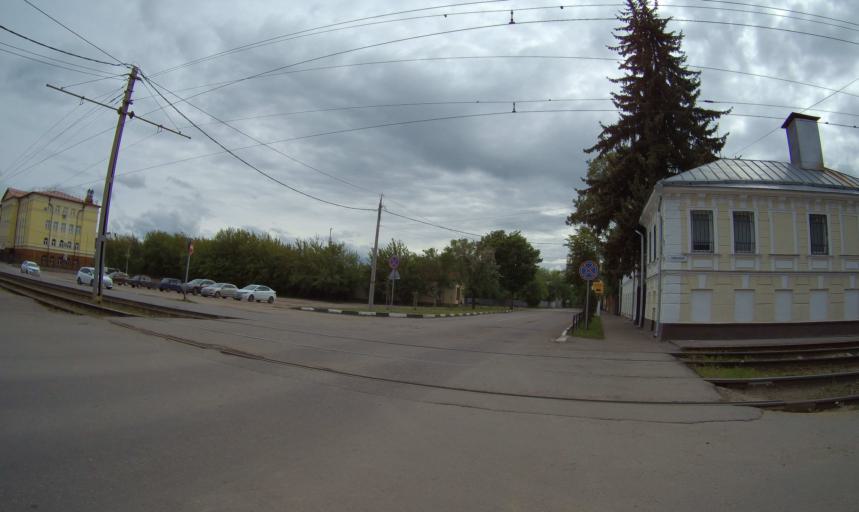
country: RU
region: Moskovskaya
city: Kolomna
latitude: 55.0979
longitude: 38.7585
